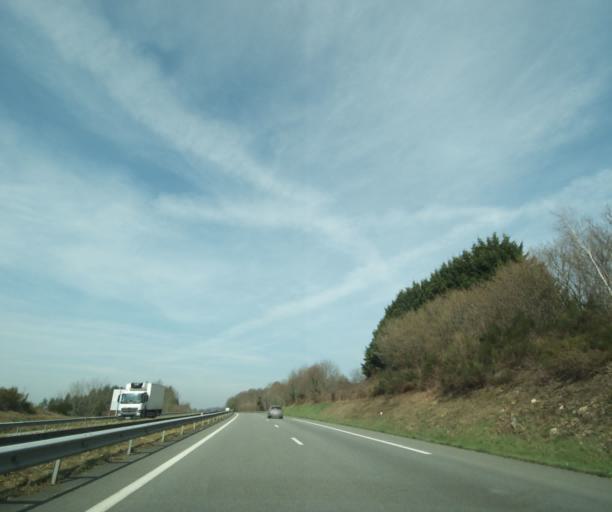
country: FR
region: Limousin
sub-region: Departement de la Correze
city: Uzerche
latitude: 45.4951
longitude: 1.5251
